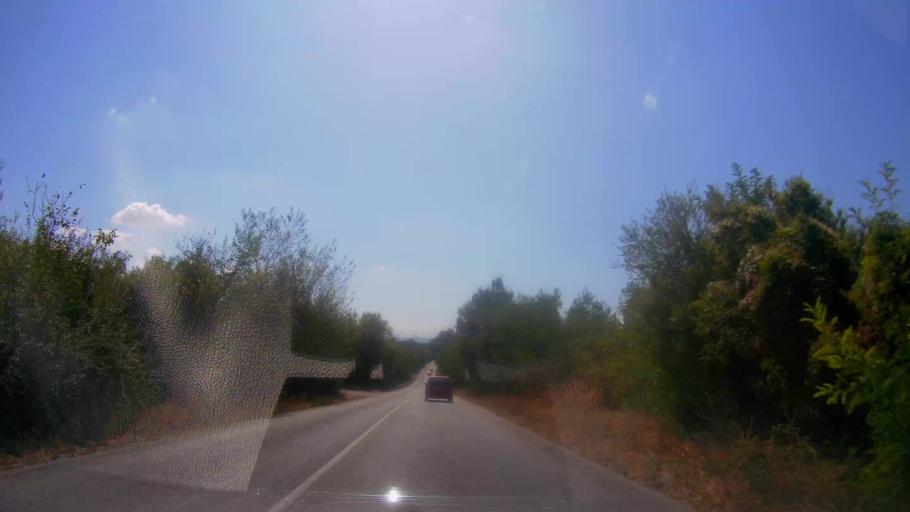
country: BG
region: Veliko Turnovo
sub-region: Obshtina Gorna Oryakhovitsa
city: Purvomaytsi
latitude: 43.2519
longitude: 25.6436
